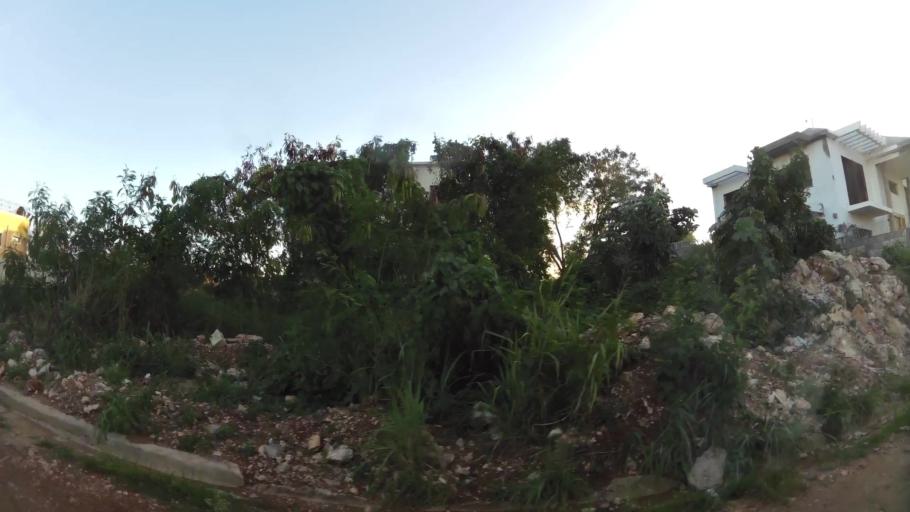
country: DO
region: Santo Domingo
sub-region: Santo Domingo
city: Santo Domingo Este
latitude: 18.4870
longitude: -69.8184
